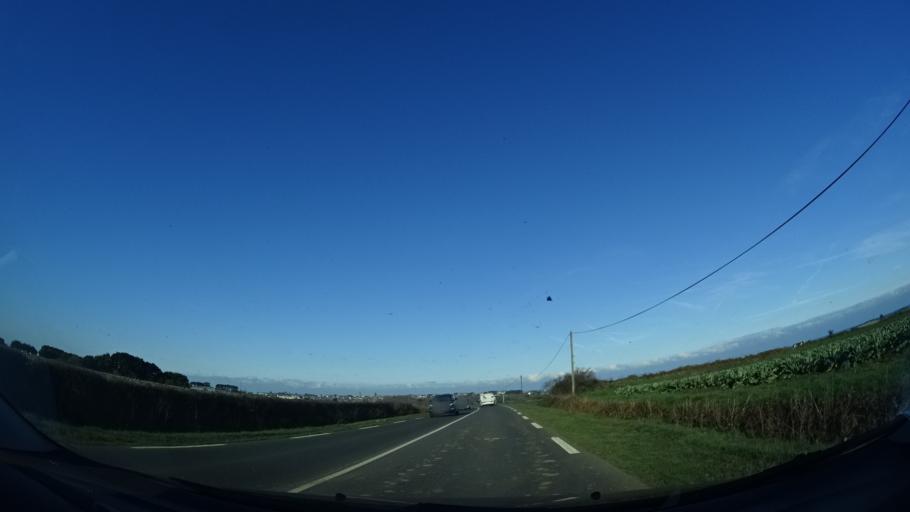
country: FR
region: Brittany
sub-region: Departement du Finistere
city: Saint-Pol-de-Leon
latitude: 48.6588
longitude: -3.9670
